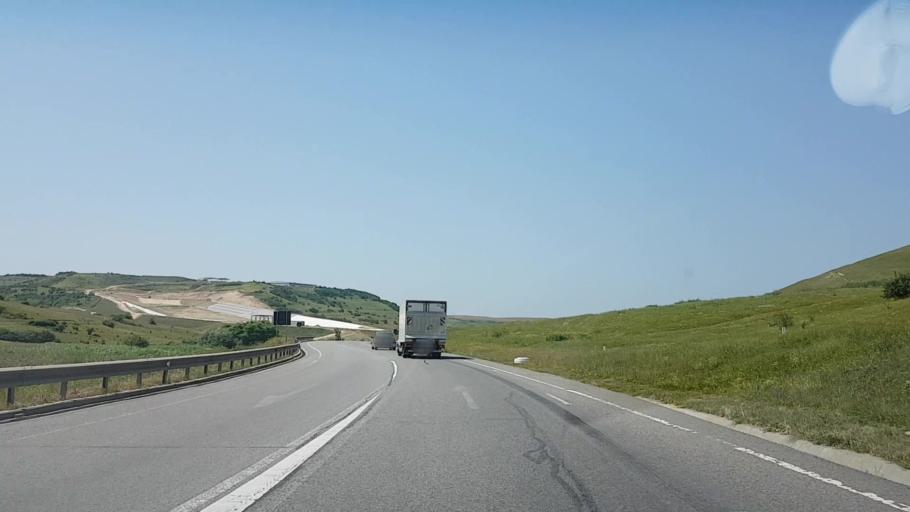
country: RO
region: Cluj
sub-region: Comuna Apahida
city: Dezmir
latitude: 46.7468
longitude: 23.7108
